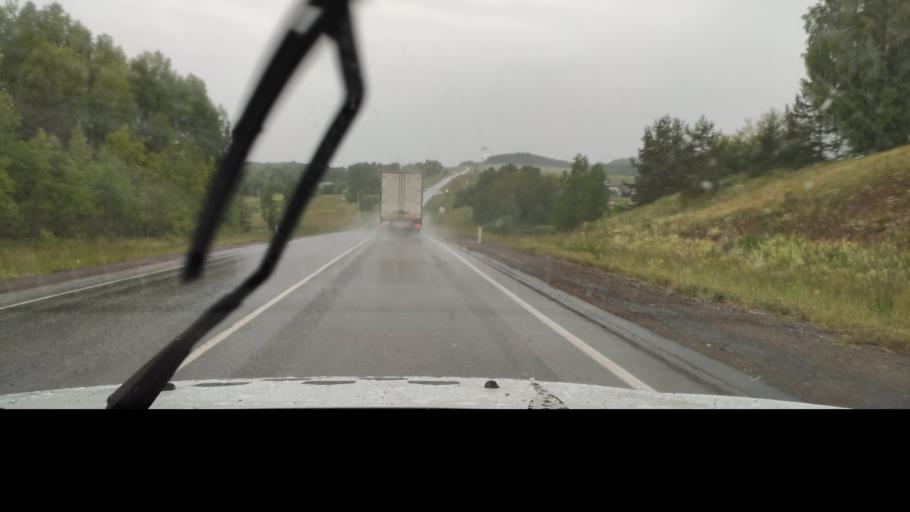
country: RU
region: Udmurtiya
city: Votkinsk
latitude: 57.3074
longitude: 54.3709
